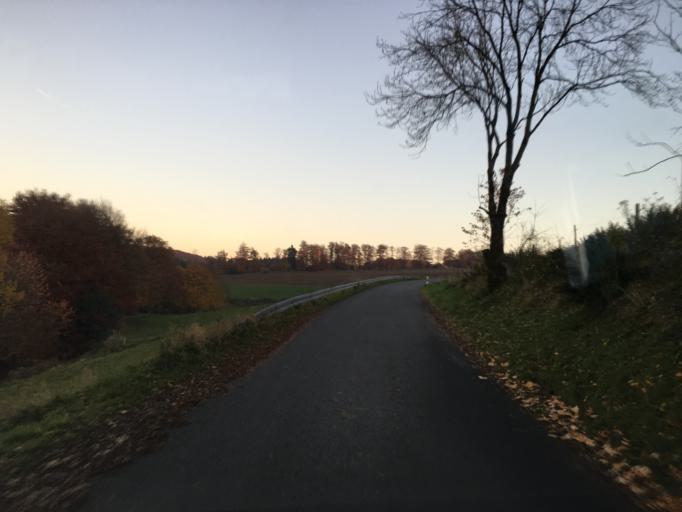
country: DE
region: North Rhine-Westphalia
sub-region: Regierungsbezirk Arnsberg
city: Nachrodt-Wiblingwerde
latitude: 51.2825
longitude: 7.5874
